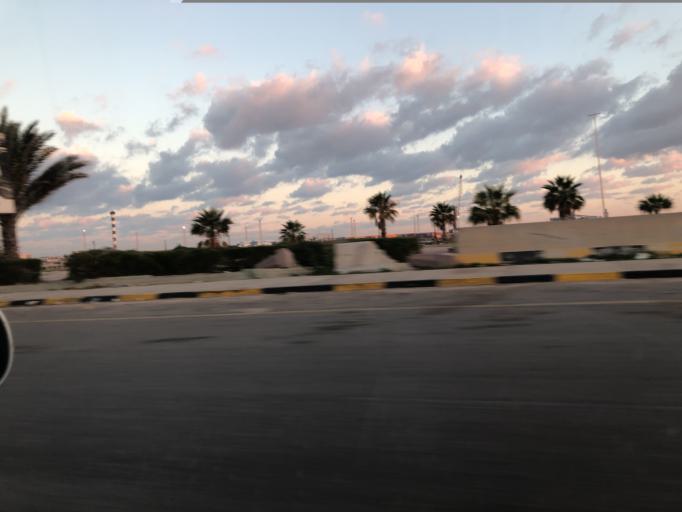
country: LY
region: Tripoli
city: Tripoli
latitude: 32.8983
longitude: 13.1814
